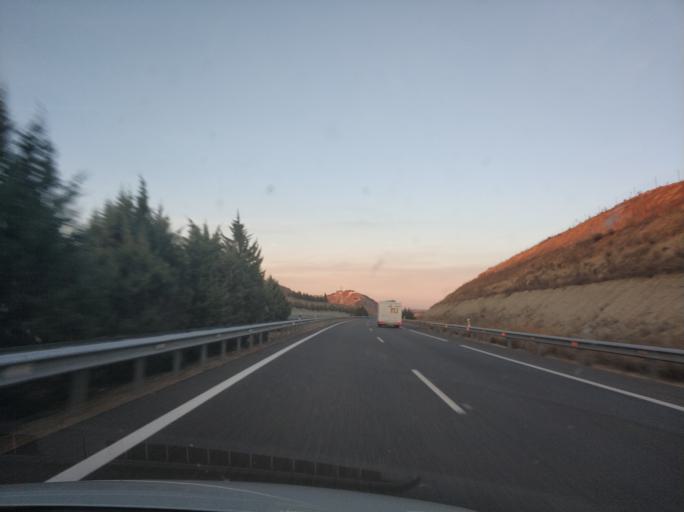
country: ES
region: Castille and Leon
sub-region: Provincia de Palencia
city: Soto de Cerrato
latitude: 41.9688
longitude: -4.4549
